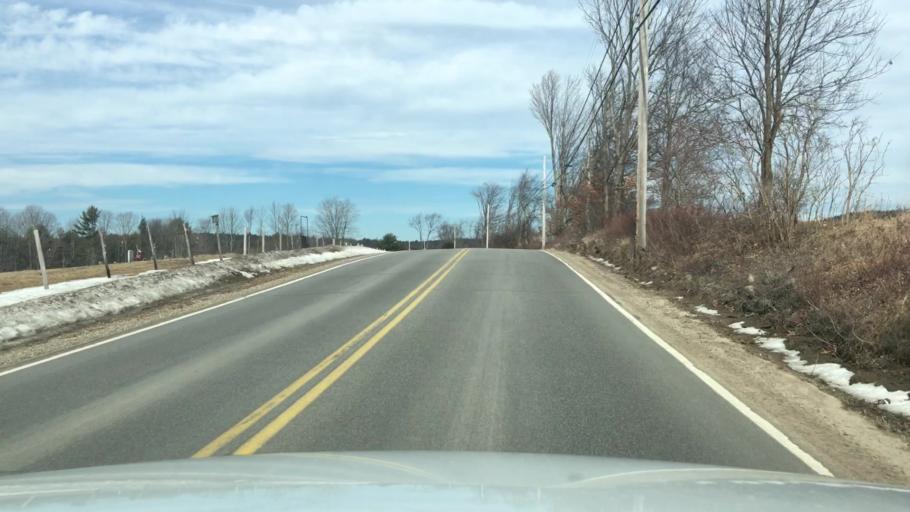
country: US
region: Maine
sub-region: York County
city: Springvale
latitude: 43.4931
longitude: -70.8089
